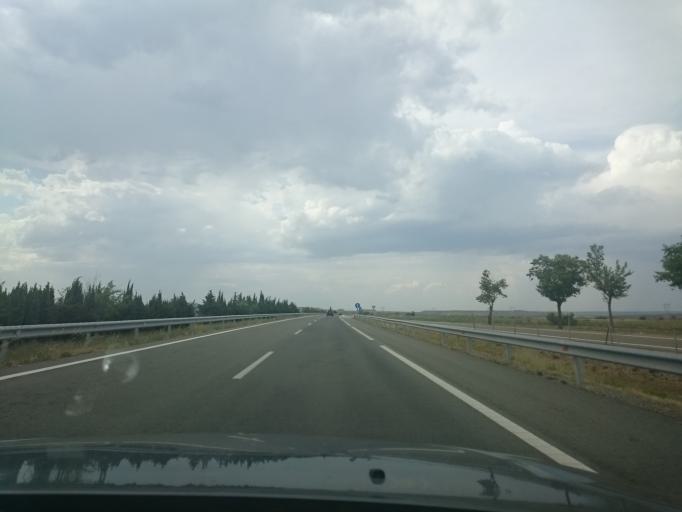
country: ES
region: Navarre
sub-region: Provincia de Navarra
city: Corella
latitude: 42.1649
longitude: -1.8263
